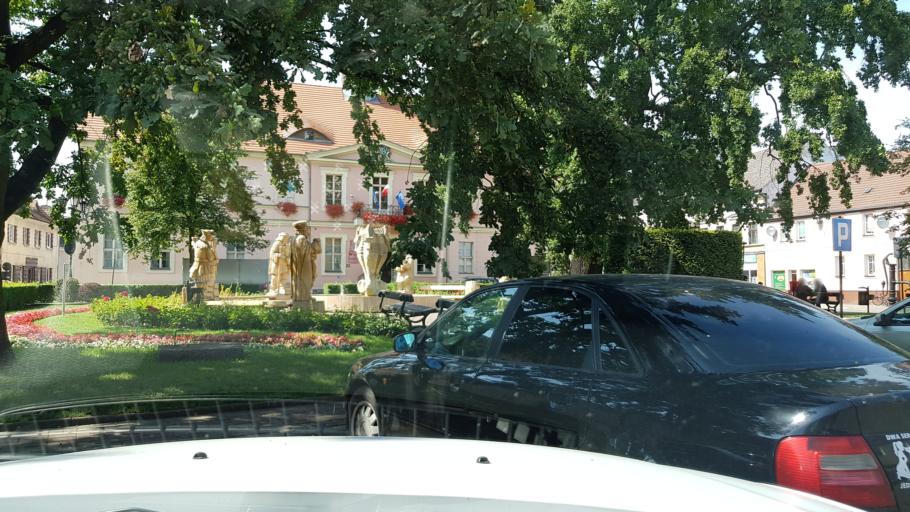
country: PL
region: West Pomeranian Voivodeship
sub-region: Powiat pyrzycki
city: Lipiany
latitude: 53.0027
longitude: 14.9699
